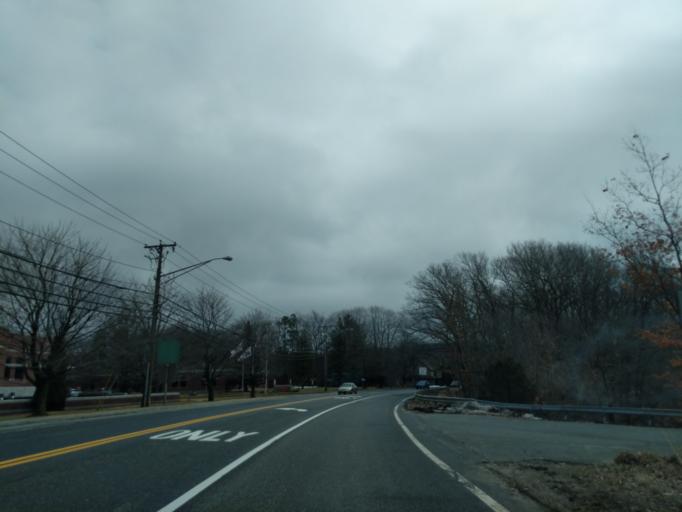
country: US
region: Massachusetts
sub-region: Worcester County
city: Webster
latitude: 42.0612
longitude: -71.8560
